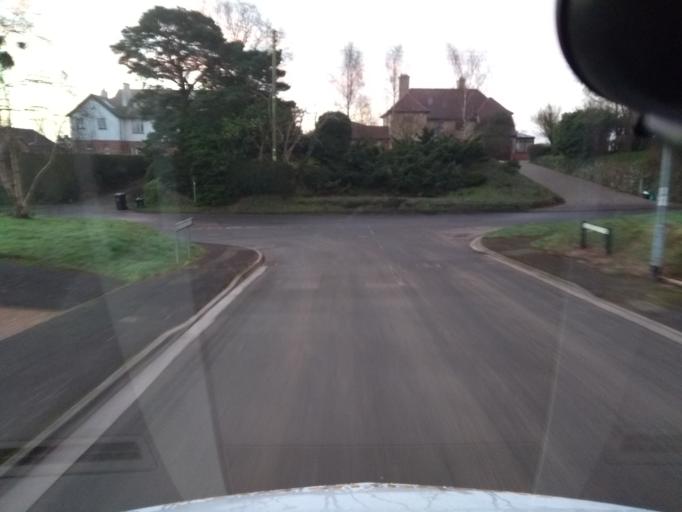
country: GB
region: England
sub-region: Somerset
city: Bridgwater
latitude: 51.1243
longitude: -3.0353
